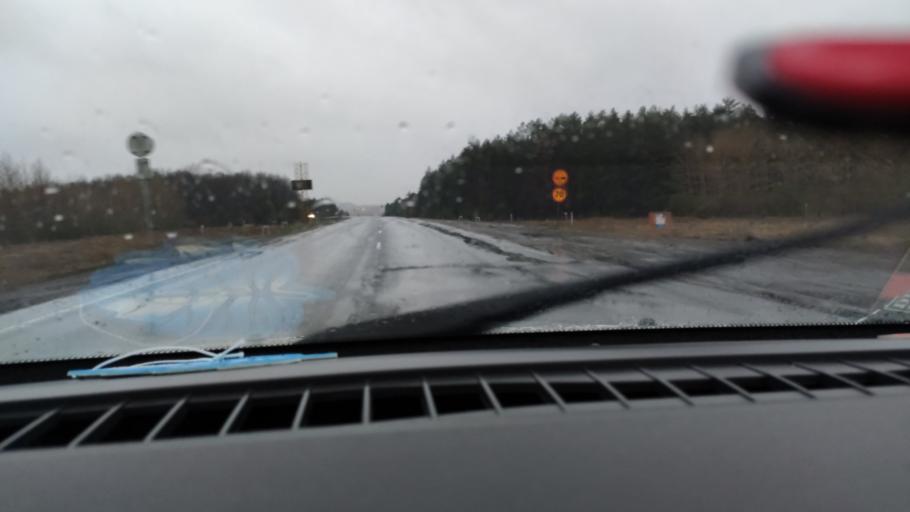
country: RU
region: Tatarstan
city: Mendeleyevsk
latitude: 55.9463
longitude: 52.2969
